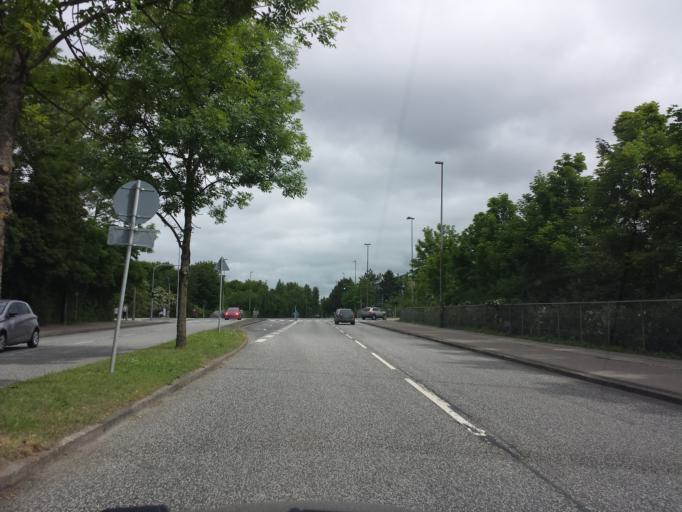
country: DK
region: Capital Region
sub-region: Ballerup Kommune
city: Ballerup
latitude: 55.7284
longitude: 12.3460
